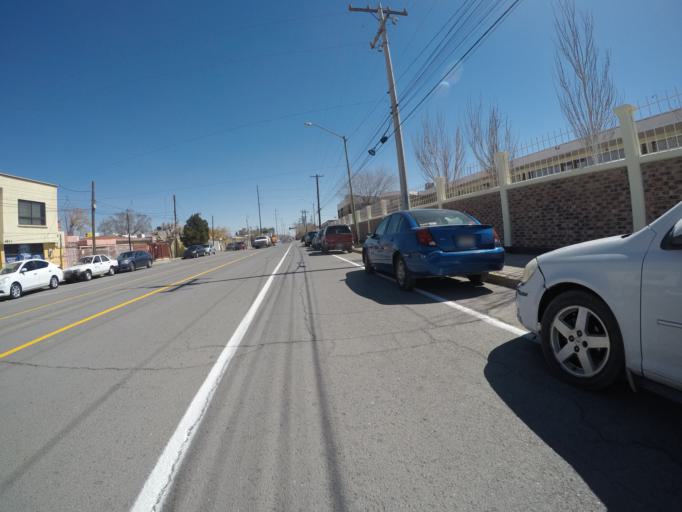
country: MX
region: Chihuahua
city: Ciudad Juarez
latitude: 31.7313
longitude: -106.4423
